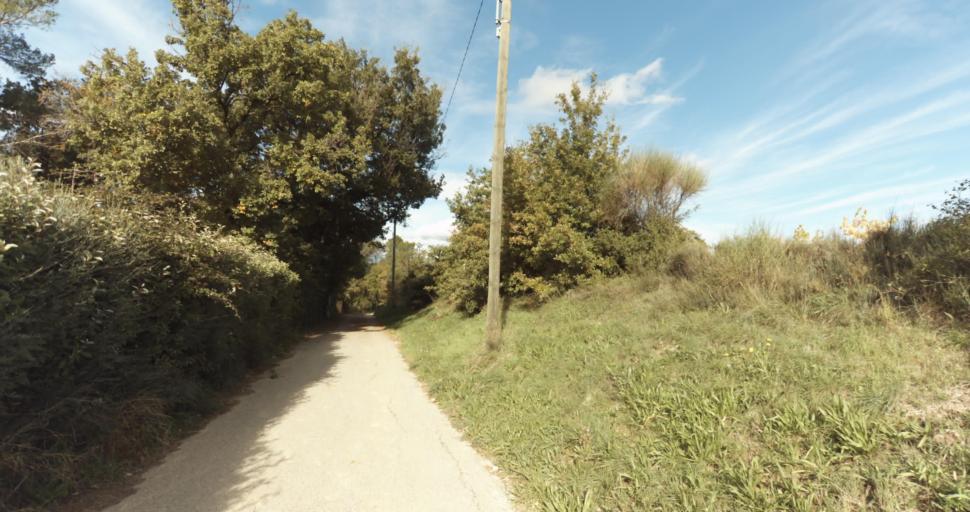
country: FR
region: Provence-Alpes-Cote d'Azur
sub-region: Departement des Bouches-du-Rhone
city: Venelles
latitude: 43.6074
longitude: 5.4860
